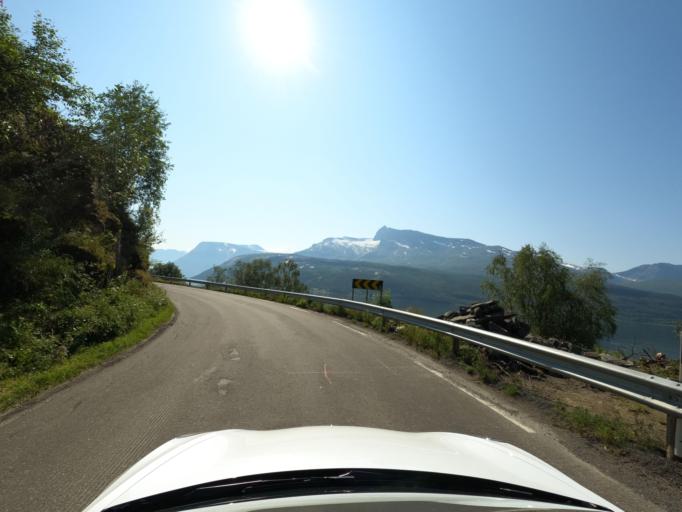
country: NO
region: Nordland
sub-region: Narvik
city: Narvik
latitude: 68.2950
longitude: 17.3561
